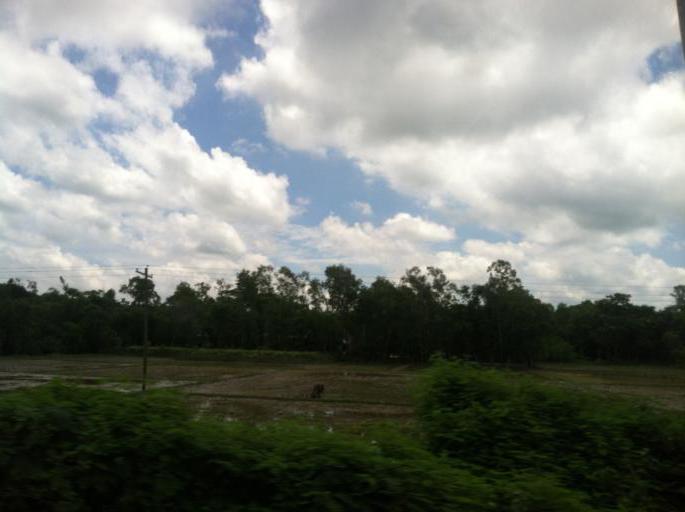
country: BD
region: Sylhet
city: Habiganj
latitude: 24.1941
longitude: 91.3506
